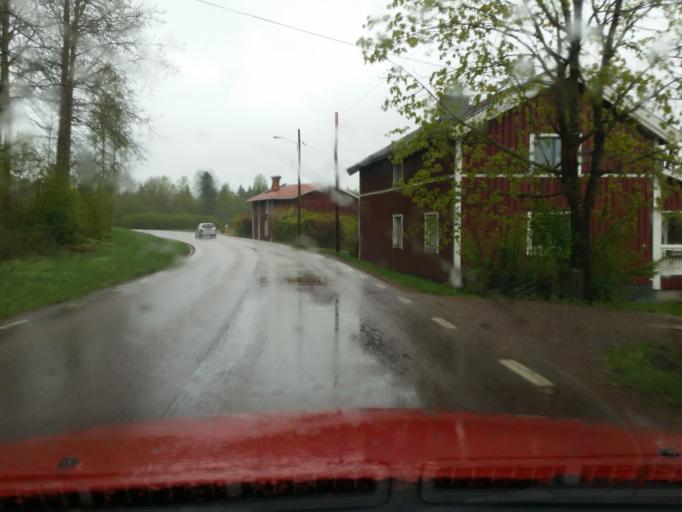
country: SE
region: Dalarna
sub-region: Saters Kommun
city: Saeter
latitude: 60.3504
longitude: 15.7793
